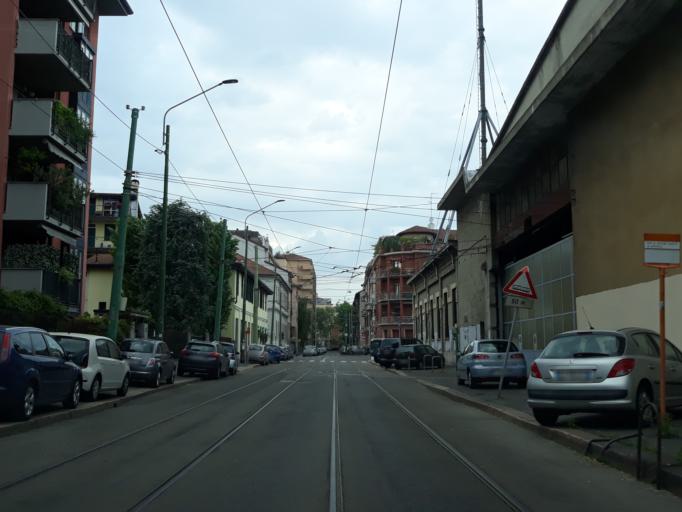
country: IT
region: Lombardy
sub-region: Citta metropolitana di Milano
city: Milano
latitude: 45.4852
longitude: 9.1711
